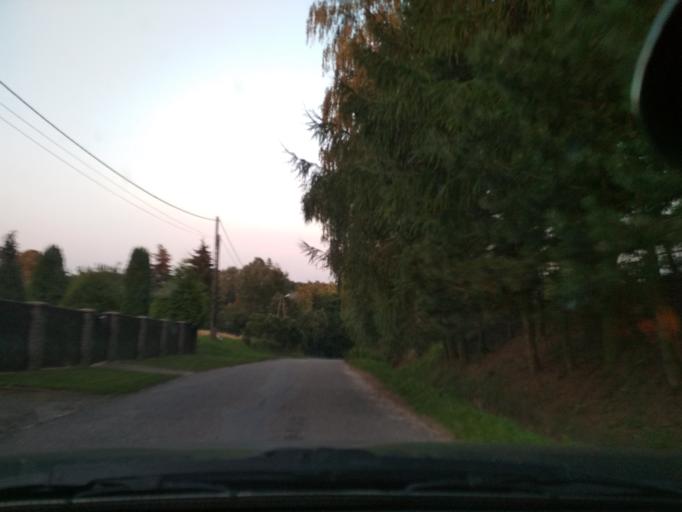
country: PL
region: Lesser Poland Voivodeship
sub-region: Powiat olkuski
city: Wolbrom
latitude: 50.4131
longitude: 19.8334
